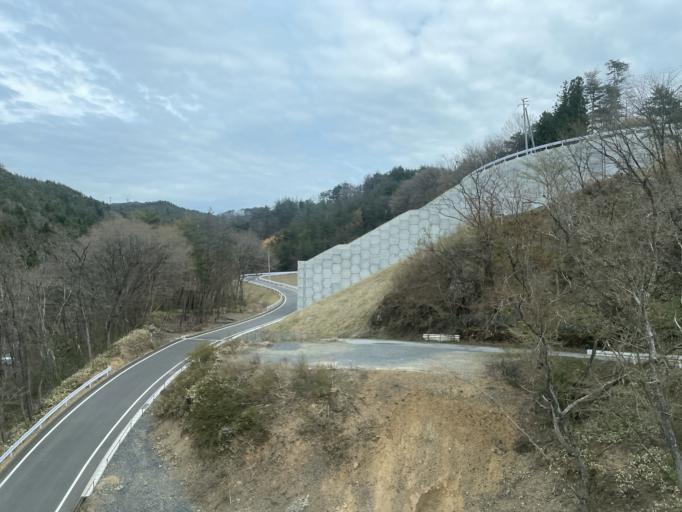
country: JP
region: Iwate
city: Ofunato
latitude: 38.9155
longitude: 141.5913
